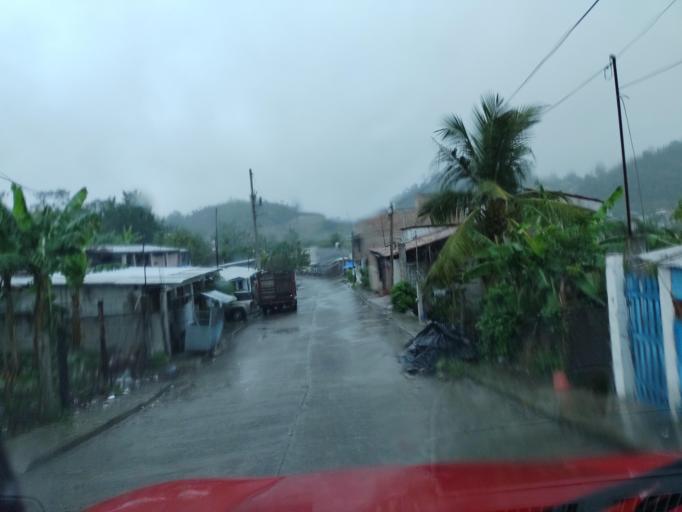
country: MX
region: Veracruz
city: Papantla de Olarte
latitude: 20.4349
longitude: -97.3378
